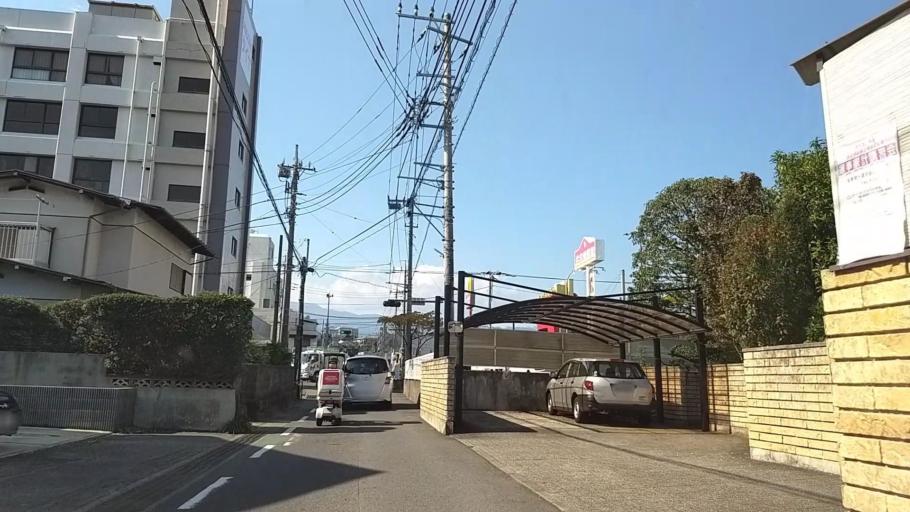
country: JP
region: Kanagawa
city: Atsugi
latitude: 35.4458
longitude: 139.3590
